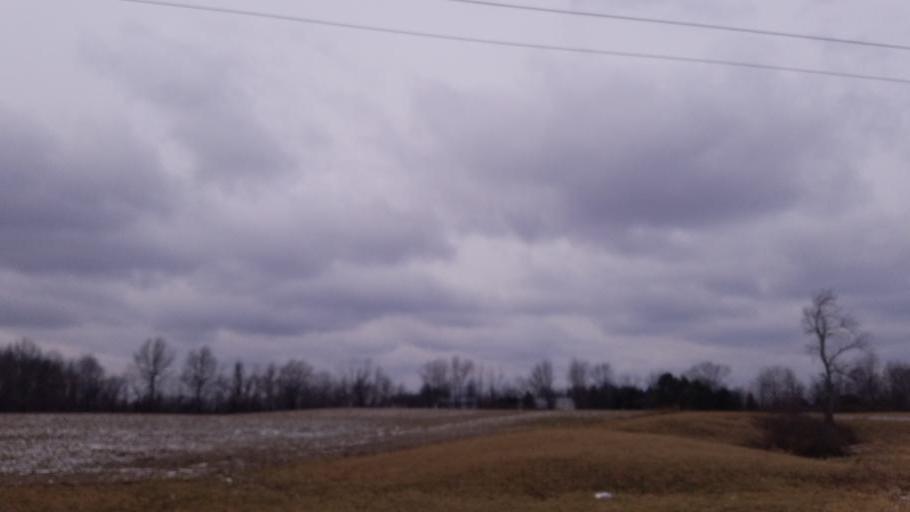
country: US
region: Ohio
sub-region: Crawford County
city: Galion
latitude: 40.6928
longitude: -82.7178
